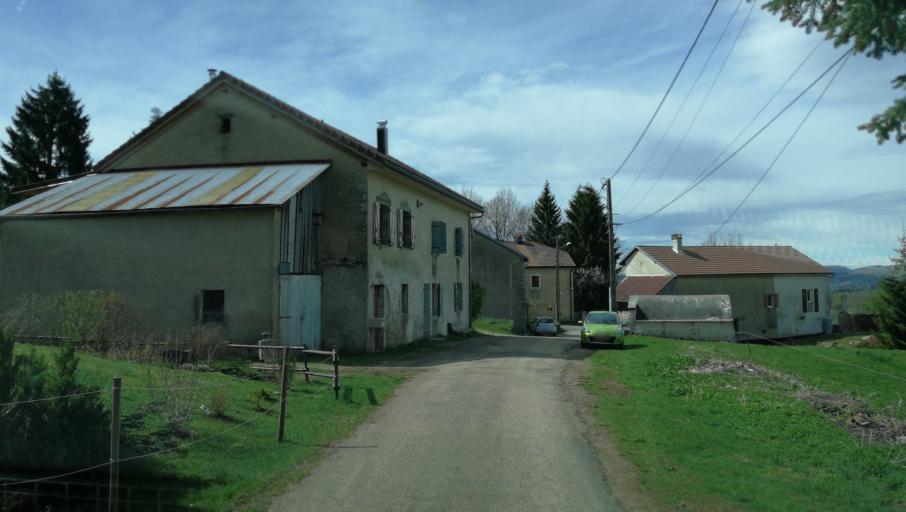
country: FR
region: Rhone-Alpes
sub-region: Departement de l'Ain
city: Chatillon-en-Michaille
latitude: 46.2550
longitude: 5.7877
